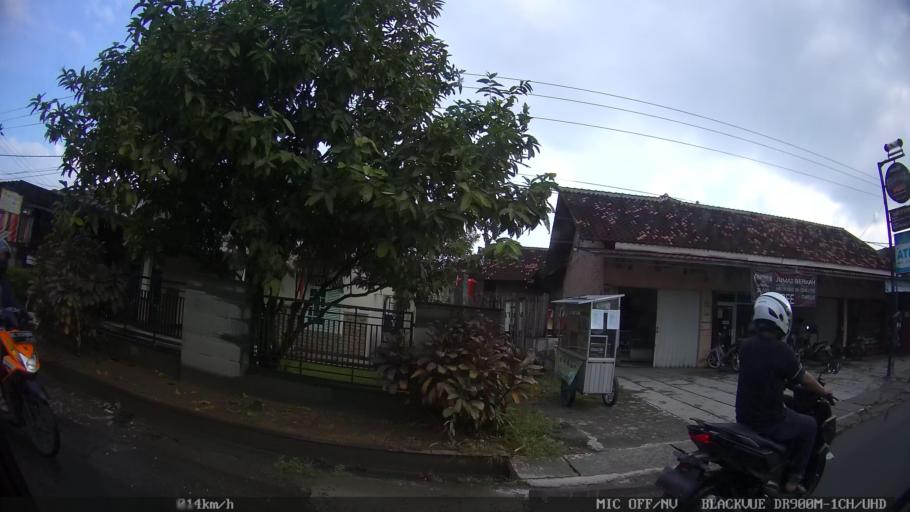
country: ID
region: Lampung
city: Kedaton
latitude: -5.3909
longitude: 105.3000
